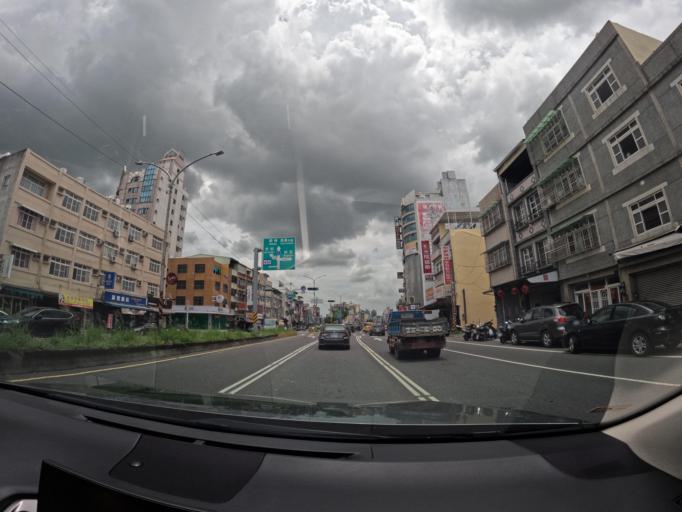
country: TW
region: Taiwan
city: Fengshan
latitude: 22.7608
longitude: 120.3091
